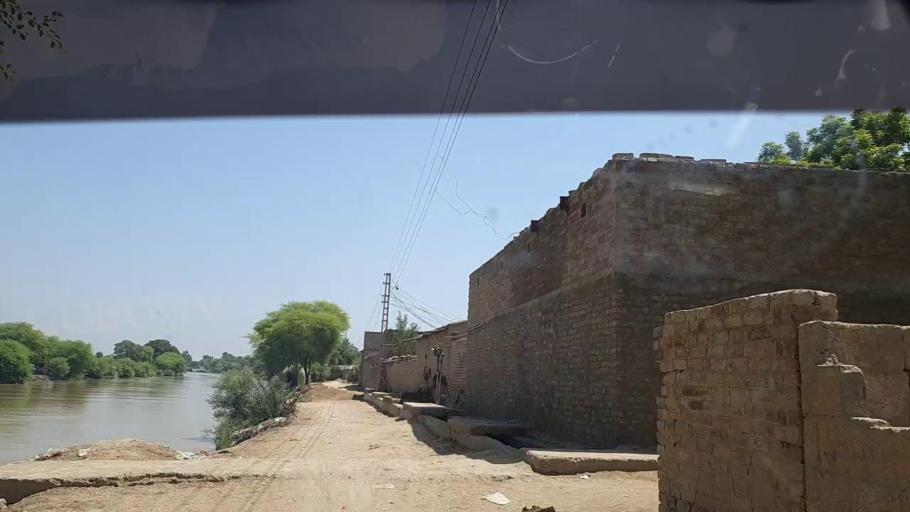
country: PK
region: Sindh
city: Ghauspur
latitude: 28.1653
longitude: 69.1294
